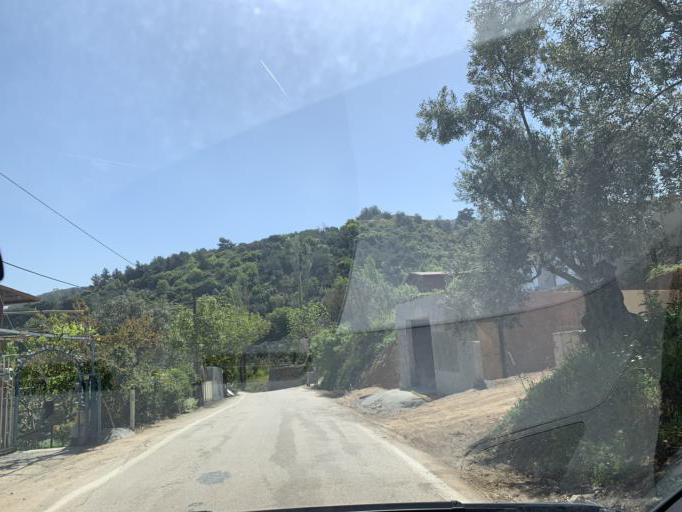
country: TR
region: Bursa
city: Niluefer
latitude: 40.3534
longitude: 28.9669
